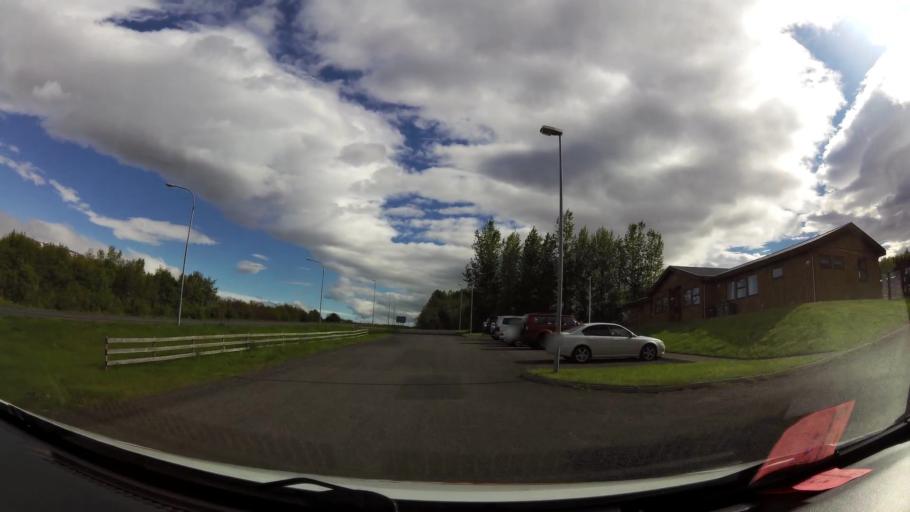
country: IS
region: Northwest
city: Saudarkrokur
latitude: 65.5515
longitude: -19.4442
